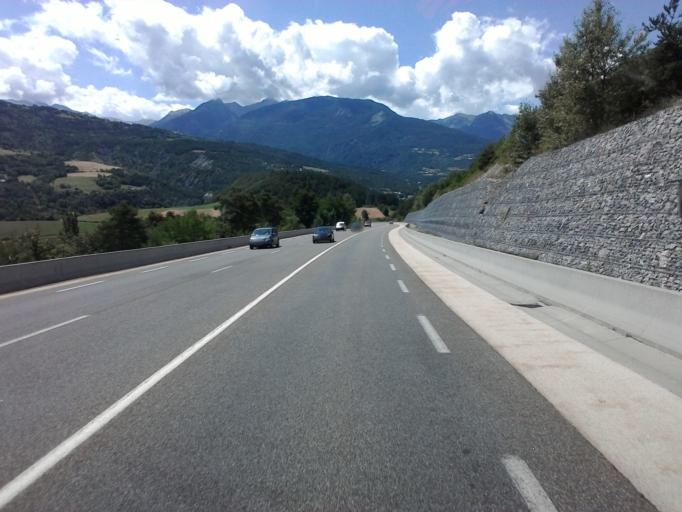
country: FR
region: Provence-Alpes-Cote d'Azur
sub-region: Departement des Hautes-Alpes
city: Embrun
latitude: 44.5744
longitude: 6.5107
